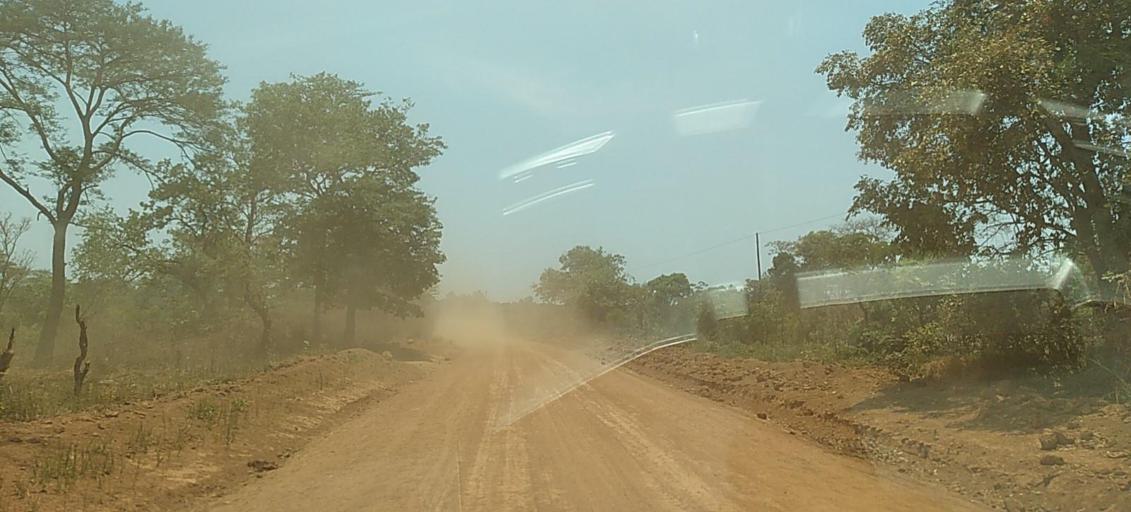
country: CD
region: Katanga
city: Kipushi
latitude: -11.8624
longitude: 27.1157
